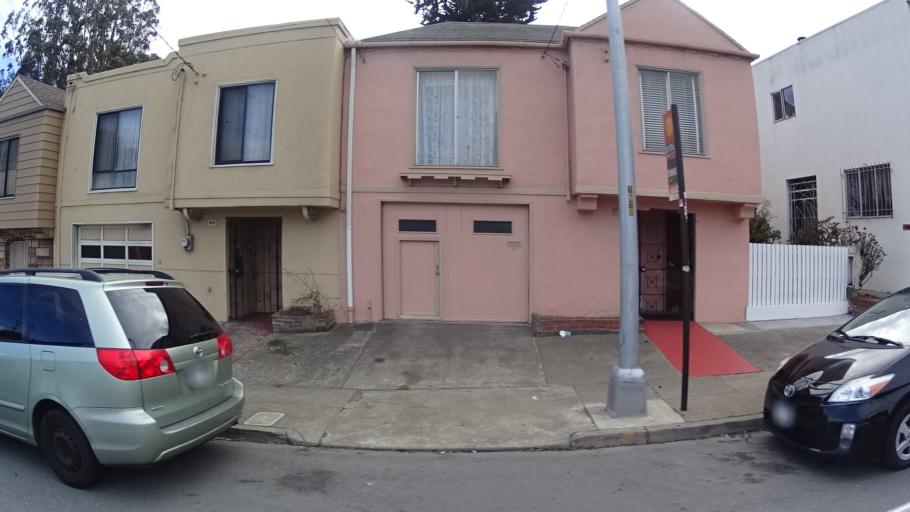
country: US
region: California
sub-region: San Mateo County
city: Daly City
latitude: 37.7116
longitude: -122.4280
